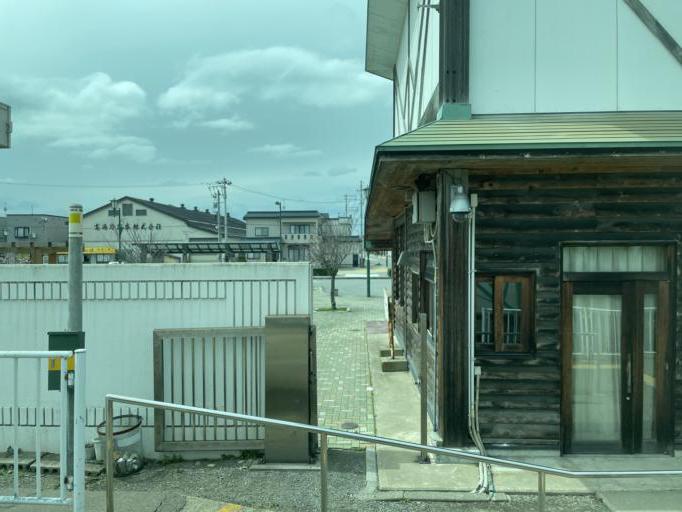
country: JP
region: Aomori
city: Goshogawara
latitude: 40.7578
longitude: 140.4354
